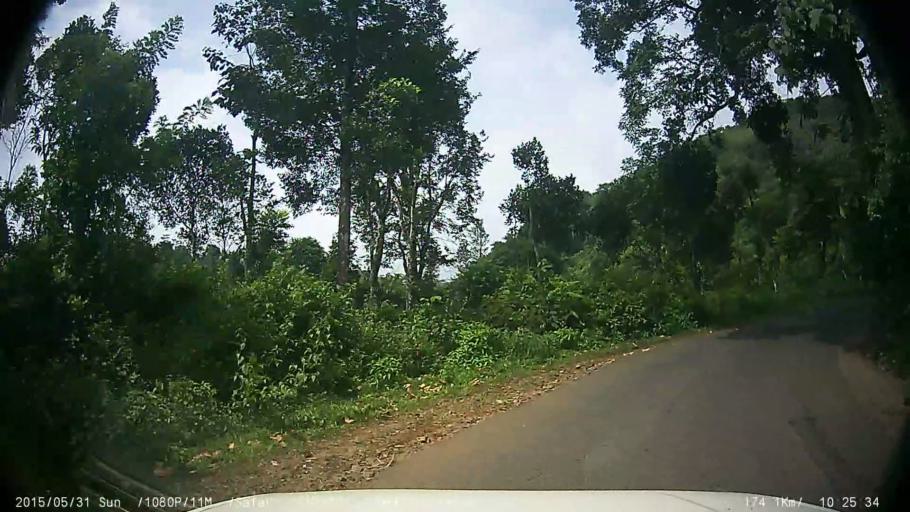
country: IN
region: Kerala
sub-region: Wayanad
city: Kalpetta
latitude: 11.5298
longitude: 76.1405
